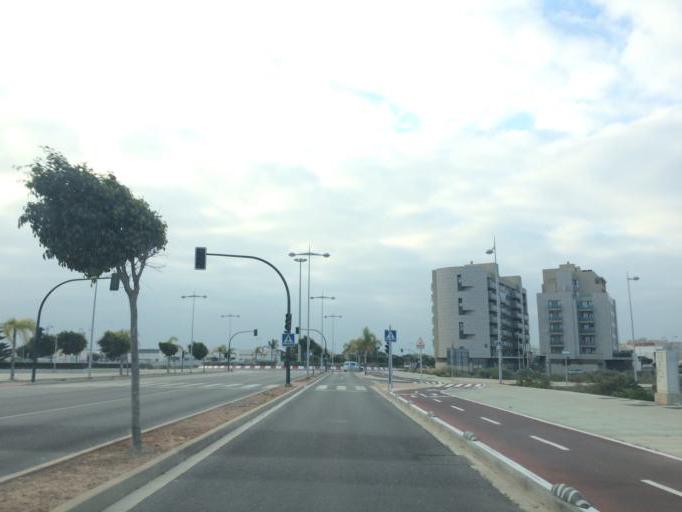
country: ES
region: Andalusia
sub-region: Provincia de Almeria
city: Almeria
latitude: 36.8292
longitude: -2.4380
